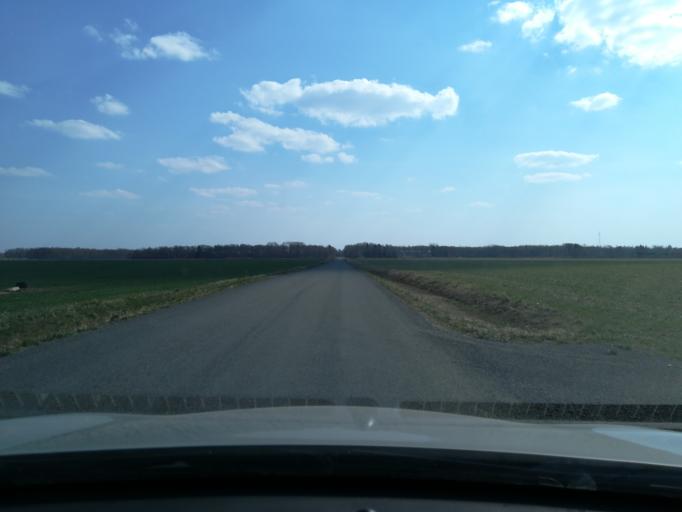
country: EE
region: Harju
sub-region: Saue linn
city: Saue
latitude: 59.3309
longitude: 24.5156
